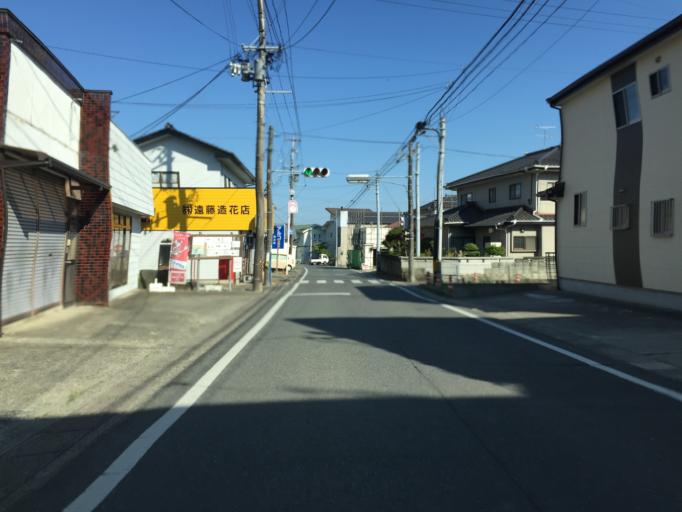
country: JP
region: Ibaraki
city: Kitaibaraki
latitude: 36.8928
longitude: 140.7566
